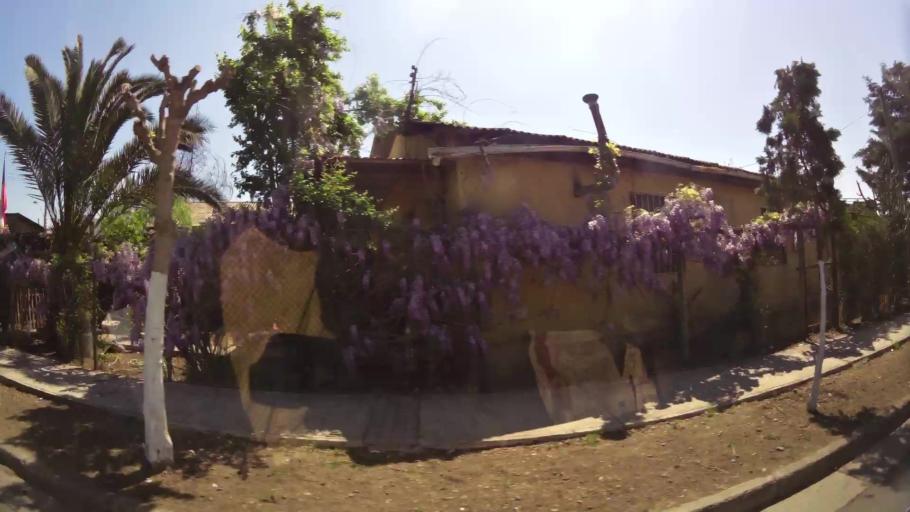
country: CL
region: Santiago Metropolitan
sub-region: Provincia de Talagante
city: Talagante
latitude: -33.6525
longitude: -70.9271
